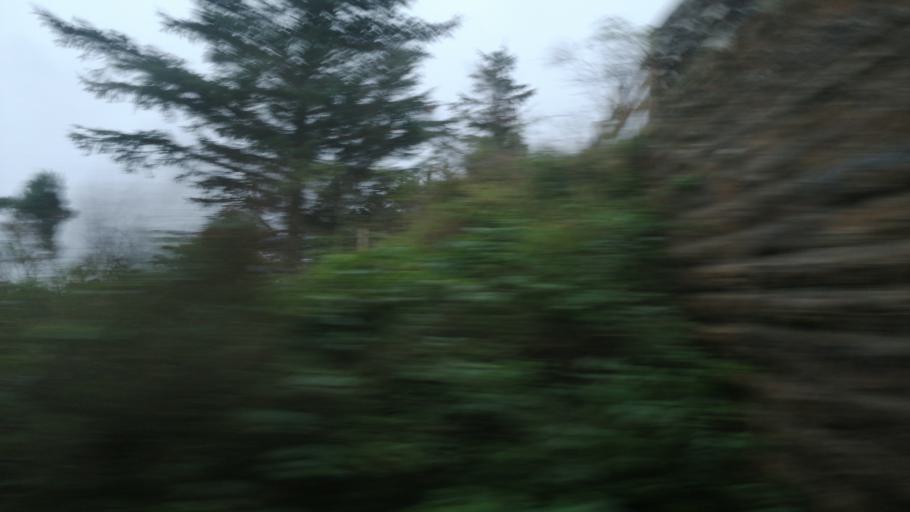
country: GB
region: Scotland
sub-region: Highland
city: Brora
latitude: 58.0286
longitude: -3.8492
